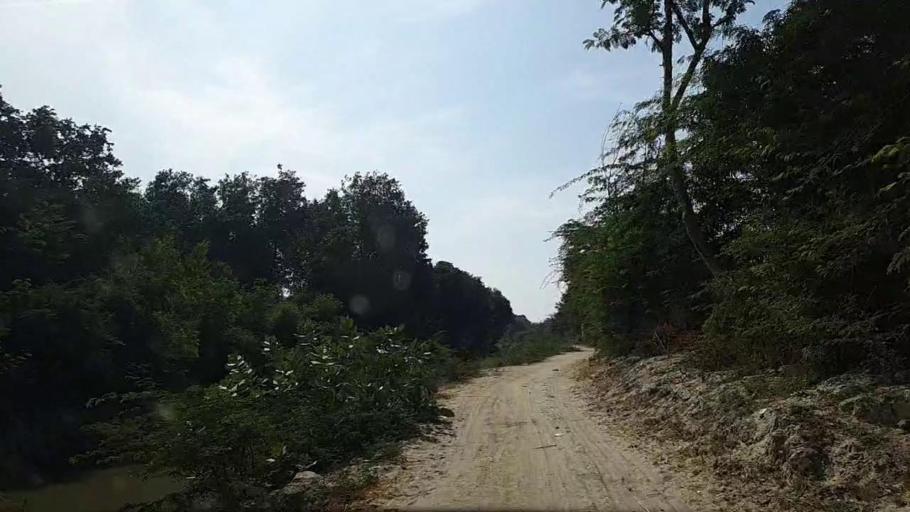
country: PK
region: Sindh
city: Daro Mehar
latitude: 24.7094
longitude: 68.1609
